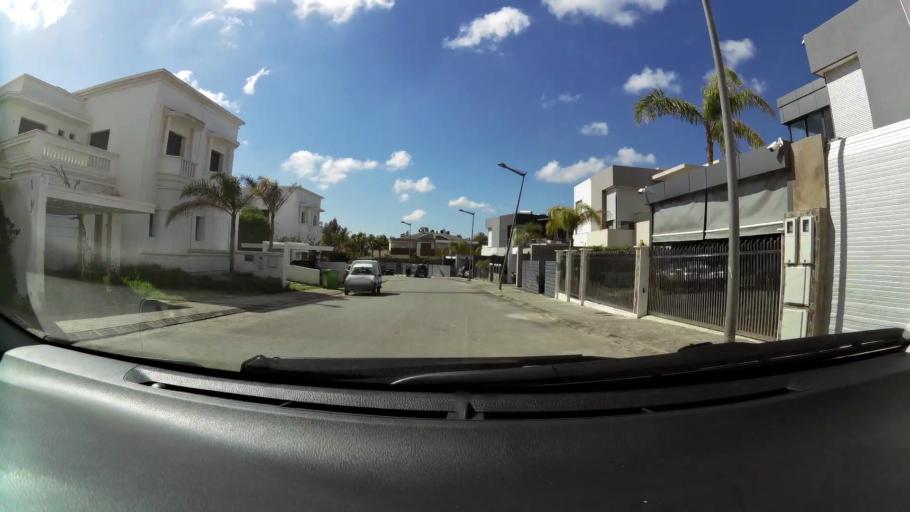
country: MA
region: Grand Casablanca
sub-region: Nouaceur
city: Bouskoura
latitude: 33.4716
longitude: -7.5998
